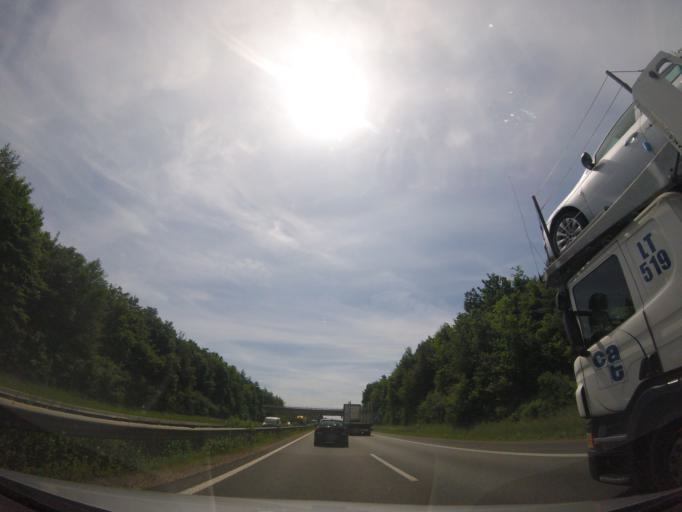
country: DE
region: Rheinland-Pfalz
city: Freimersheim
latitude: 49.7186
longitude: 8.0760
